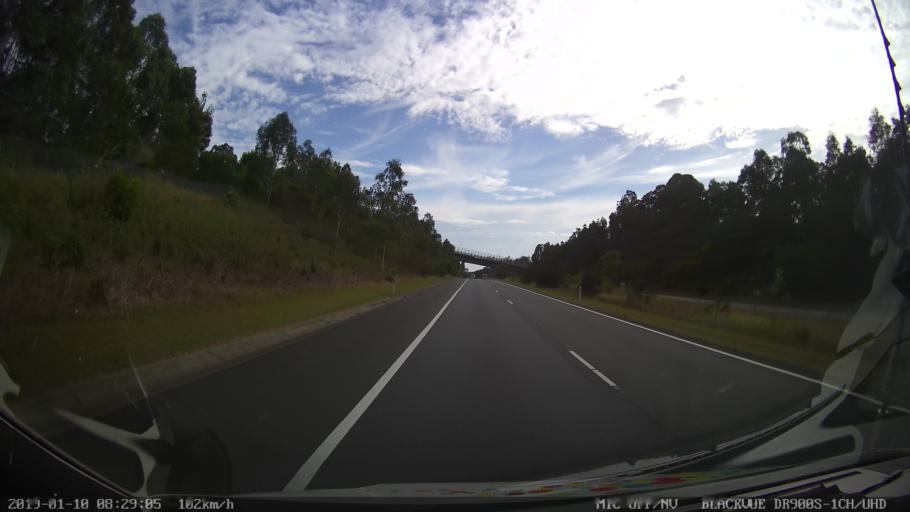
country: AU
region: New South Wales
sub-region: Coffs Harbour
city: Bonville
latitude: -30.3866
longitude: 153.0409
